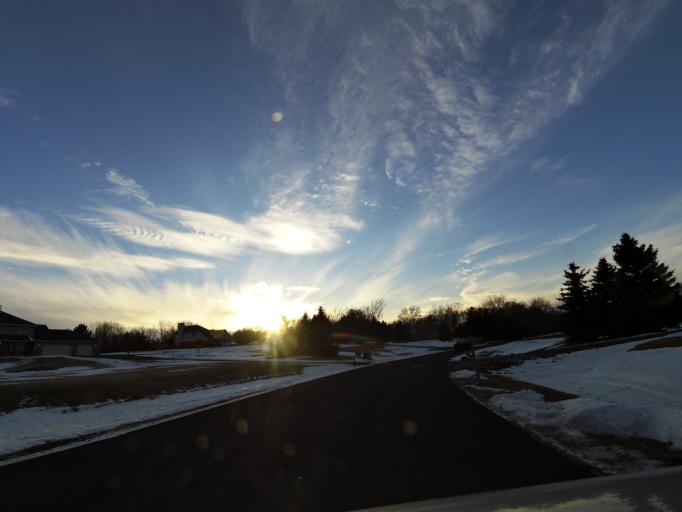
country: US
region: Minnesota
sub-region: Washington County
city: Lake Elmo
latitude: 44.9792
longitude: -92.8602
